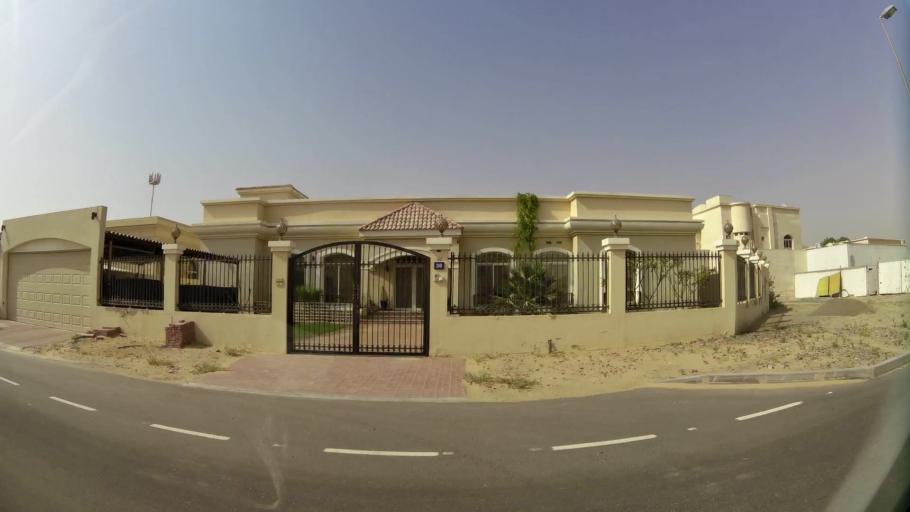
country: AE
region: Ash Shariqah
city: Sharjah
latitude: 25.2676
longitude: 55.4617
